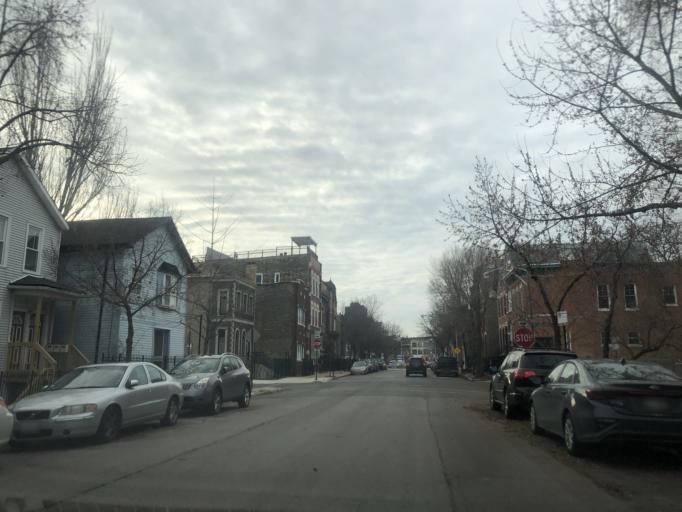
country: US
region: Illinois
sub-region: Cook County
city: Chicago
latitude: 41.9089
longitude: -87.6701
